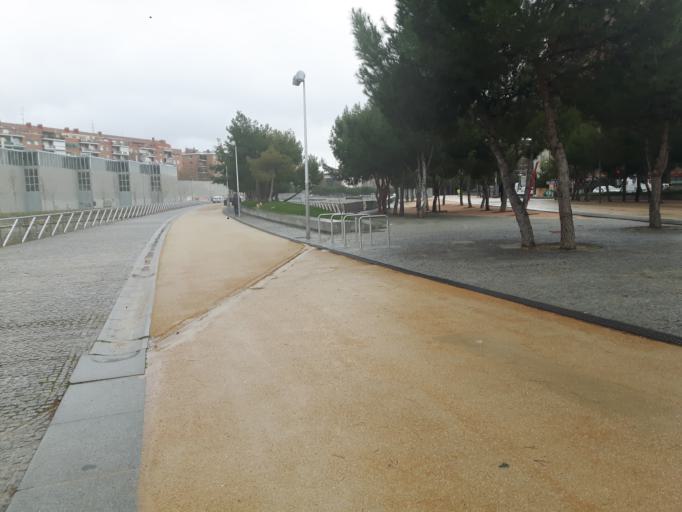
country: ES
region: Madrid
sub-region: Provincia de Madrid
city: Carabanchel
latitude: 40.4117
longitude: -3.7229
